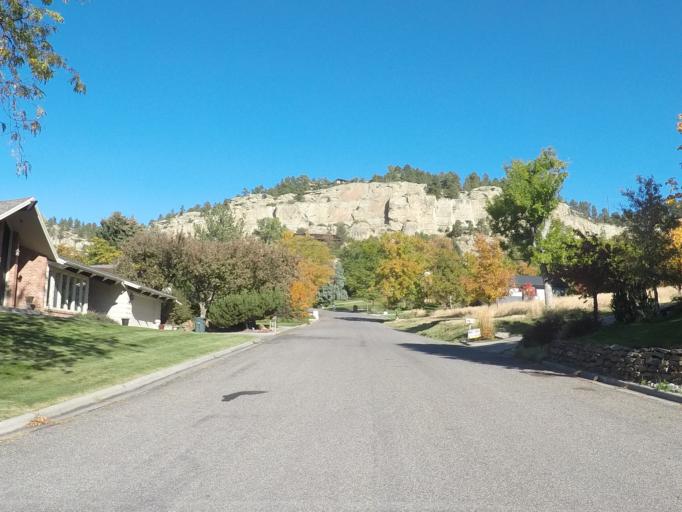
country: US
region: Montana
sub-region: Yellowstone County
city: Billings
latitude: 45.8002
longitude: -108.5831
